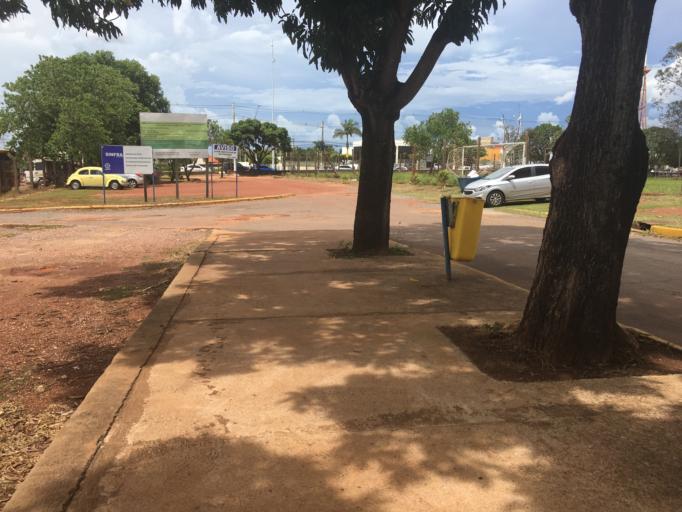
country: BR
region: Mato Grosso
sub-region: Cuiaba
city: Cuiaba
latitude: -15.6080
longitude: -56.0601
